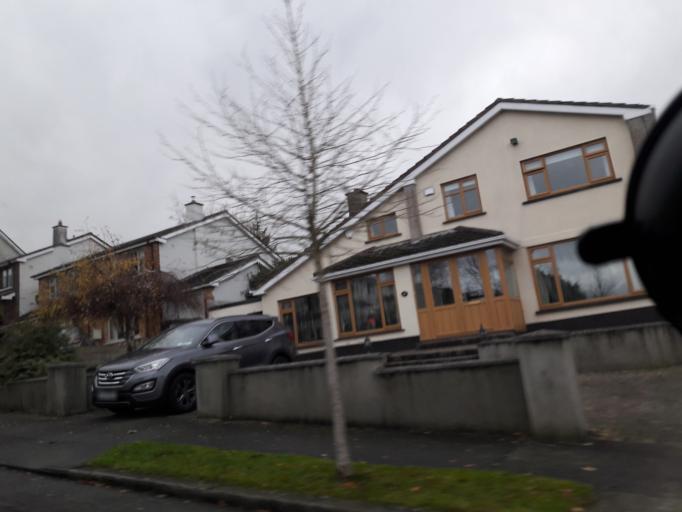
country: IE
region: Leinster
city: Malahide
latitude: 53.4456
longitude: -6.1447
